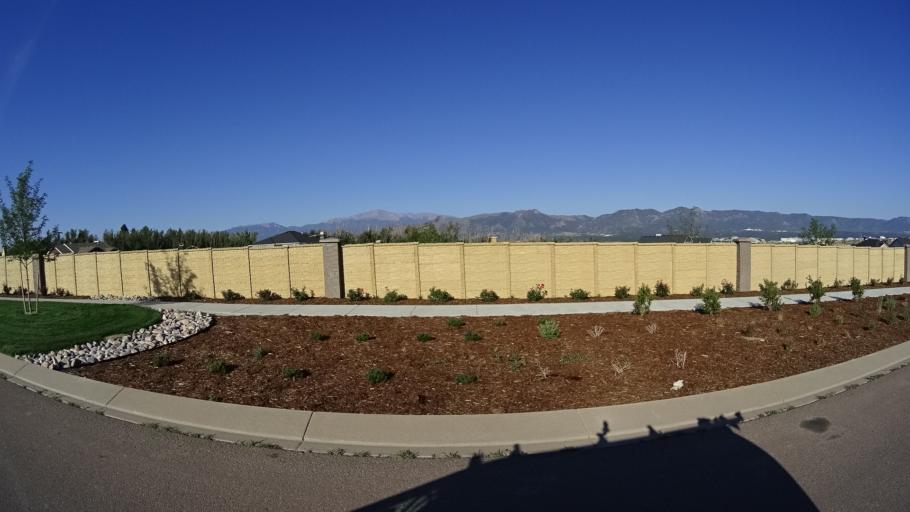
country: US
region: Colorado
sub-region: El Paso County
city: Black Forest
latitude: 38.9845
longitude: -104.7735
